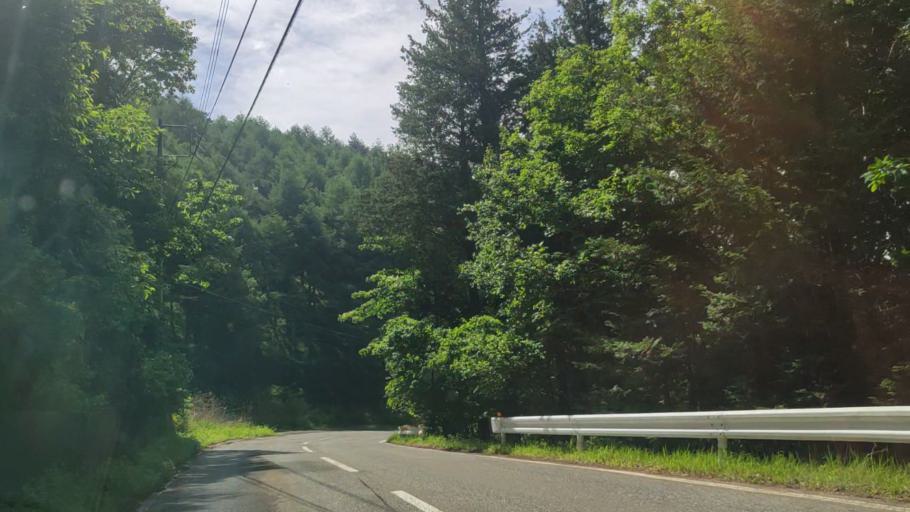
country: JP
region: Nagano
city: Suwa
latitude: 36.0928
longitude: 138.1448
